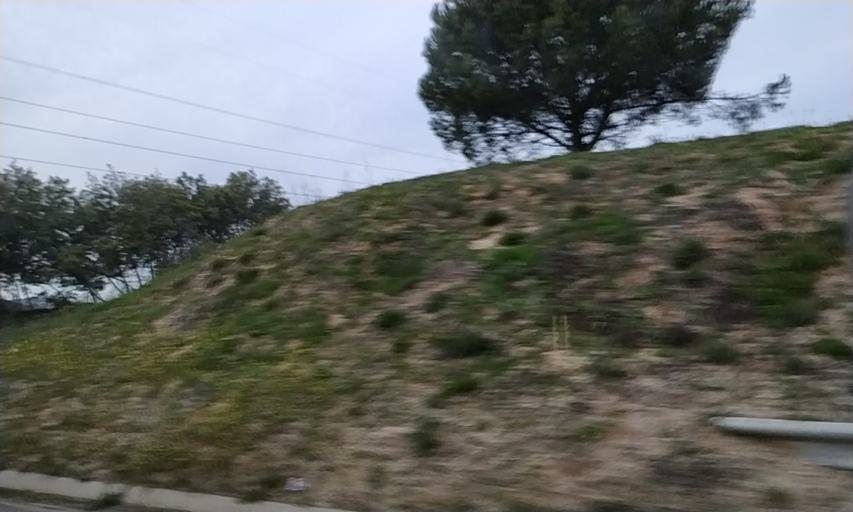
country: PT
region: Setubal
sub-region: Setubal
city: Setubal
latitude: 38.5240
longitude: -8.8438
